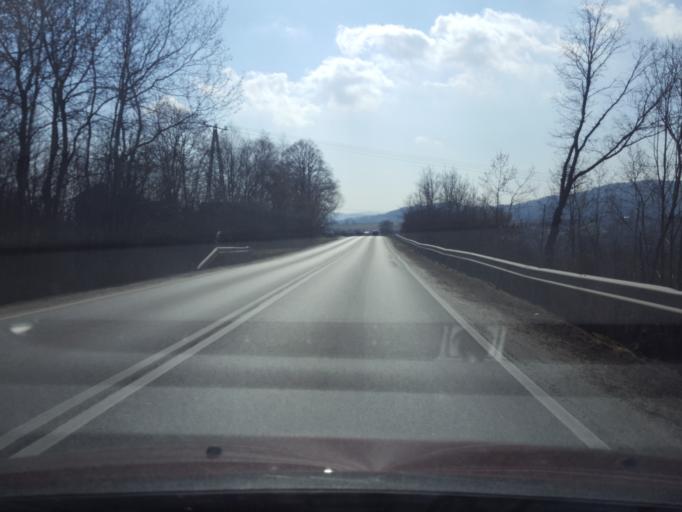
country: PL
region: Lesser Poland Voivodeship
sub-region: Powiat brzeski
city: Gnojnik
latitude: 49.8593
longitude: 20.6235
